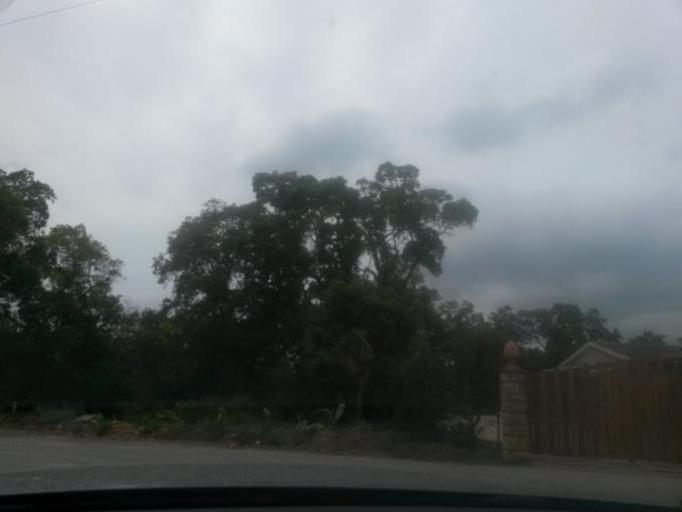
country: IT
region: Tuscany
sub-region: Provincia di Livorno
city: Porto Azzurro
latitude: 42.7473
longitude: 10.3997
